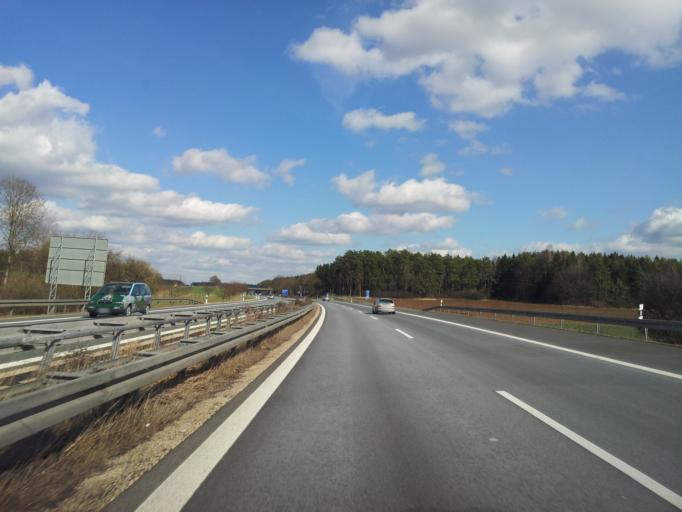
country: DE
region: Bavaria
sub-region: Upper Franconia
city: Wattendorf
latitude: 49.9871
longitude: 11.1122
